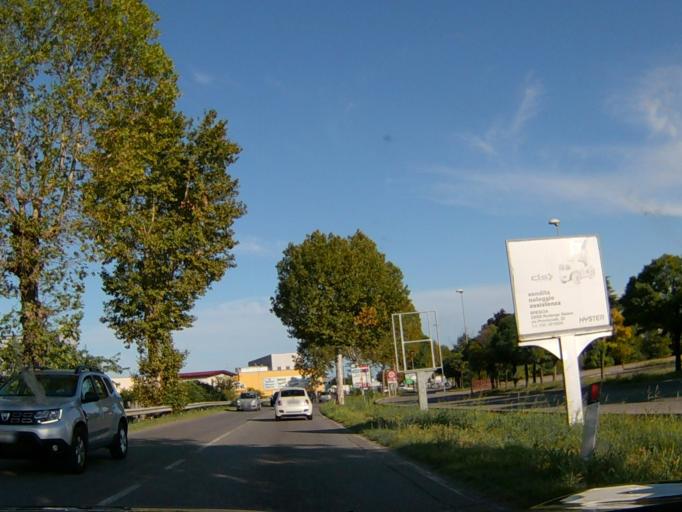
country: IT
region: Lombardy
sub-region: Provincia di Brescia
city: Molinetto
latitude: 45.4832
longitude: 10.3821
